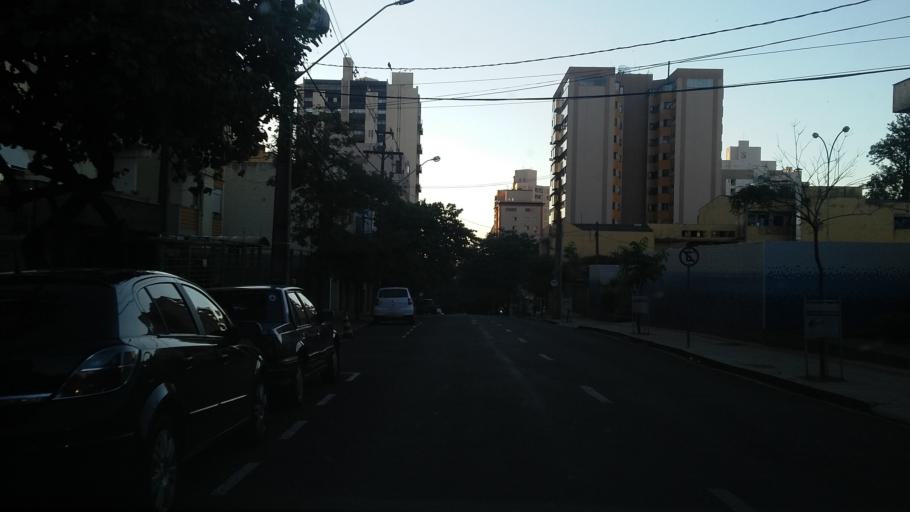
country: BR
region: Parana
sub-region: Londrina
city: Londrina
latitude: -23.3098
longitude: -51.1658
